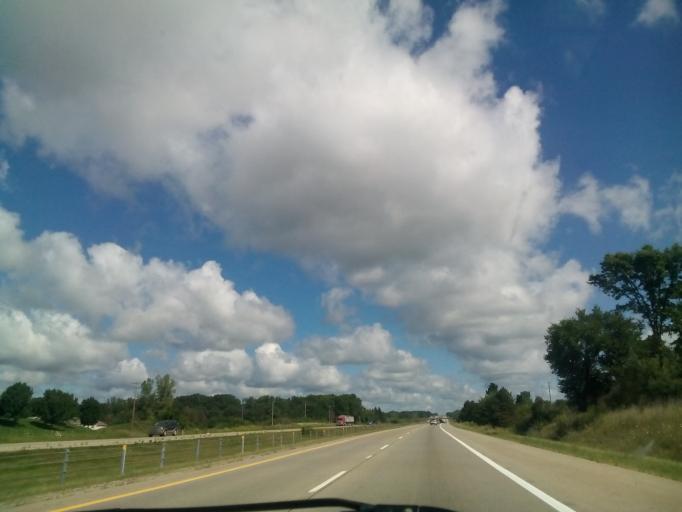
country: US
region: Michigan
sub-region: Genesee County
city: Fenton
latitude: 42.6966
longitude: -83.7612
